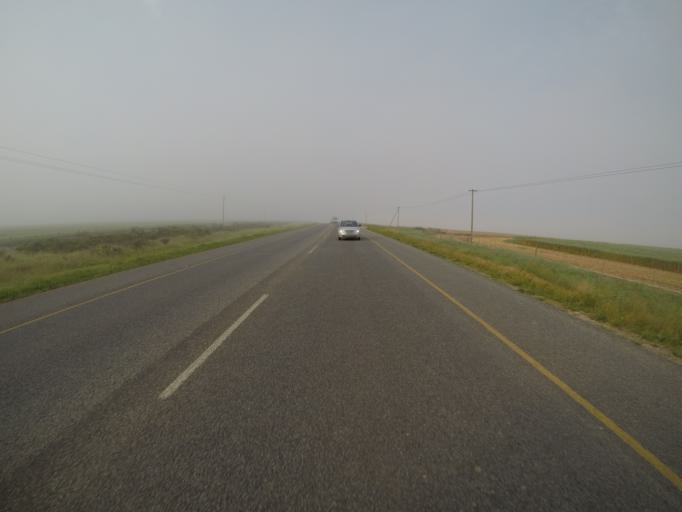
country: ZA
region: Western Cape
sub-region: West Coast District Municipality
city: Malmesbury
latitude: -33.6480
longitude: 18.7118
